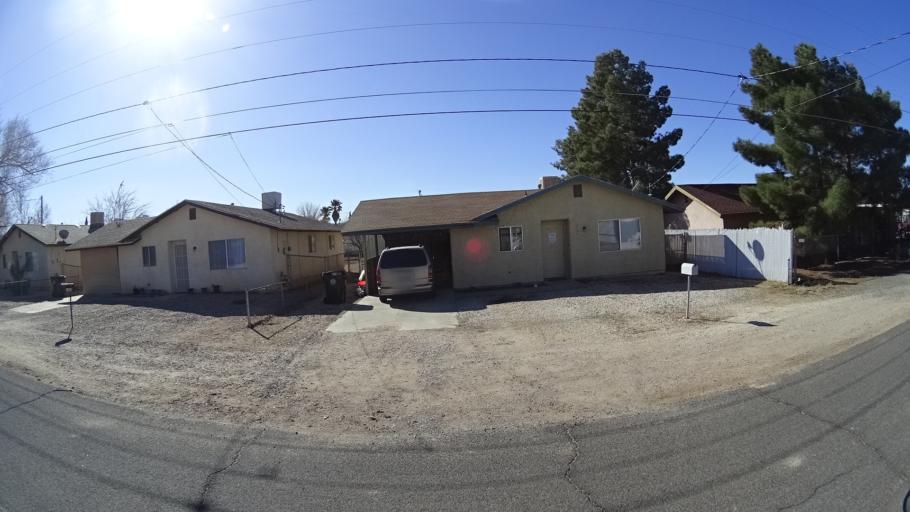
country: US
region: Arizona
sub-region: Mohave County
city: Kingman
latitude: 35.1972
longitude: -114.0213
